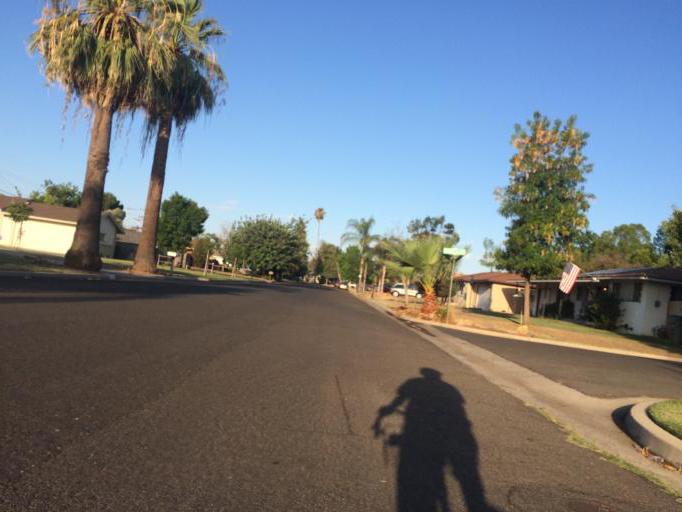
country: US
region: California
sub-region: Fresno County
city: Tarpey Village
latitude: 36.7949
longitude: -119.6968
